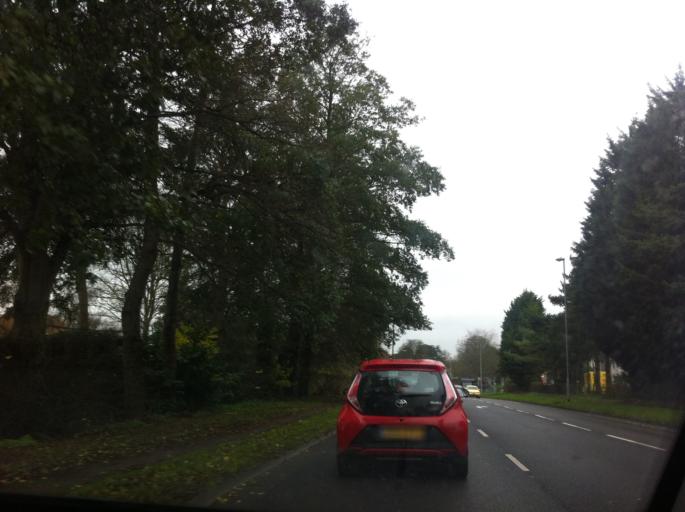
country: GB
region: England
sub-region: Northamptonshire
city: Earls Barton
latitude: 52.2649
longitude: -0.7386
